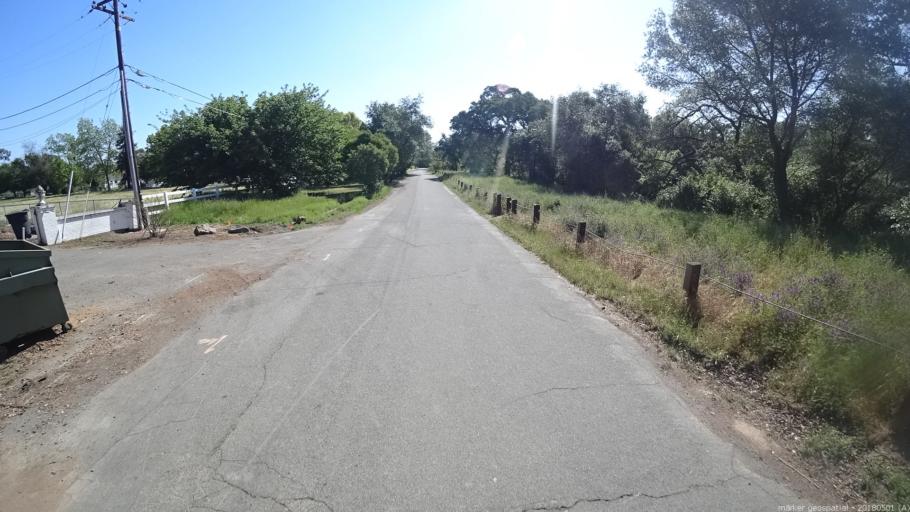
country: US
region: California
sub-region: Sacramento County
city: Foothill Farms
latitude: 38.6436
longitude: -121.3699
